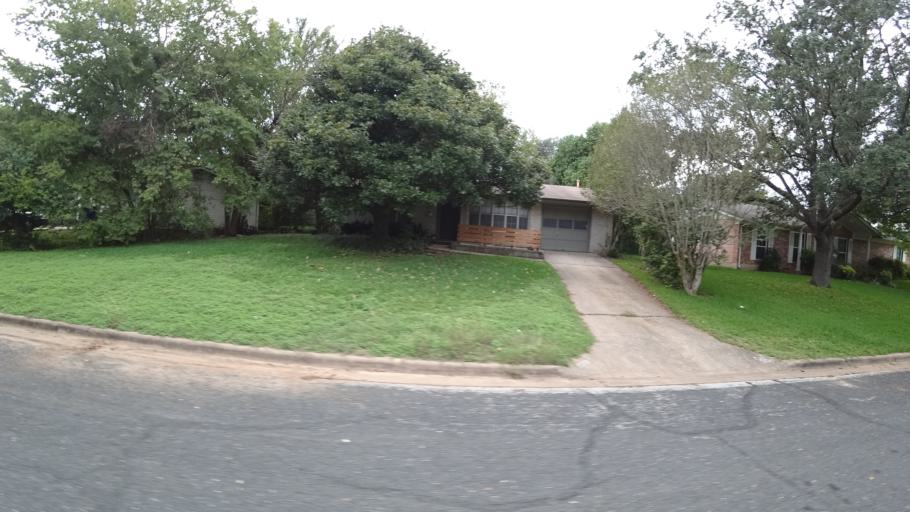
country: US
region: Texas
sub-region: Travis County
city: Rollingwood
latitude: 30.2187
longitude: -97.7918
